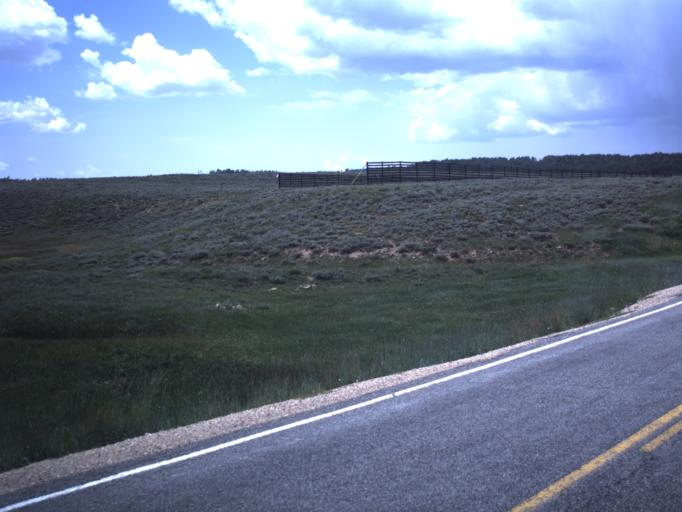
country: US
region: Utah
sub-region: Sanpete County
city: Fairview
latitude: 39.6662
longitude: -111.3030
